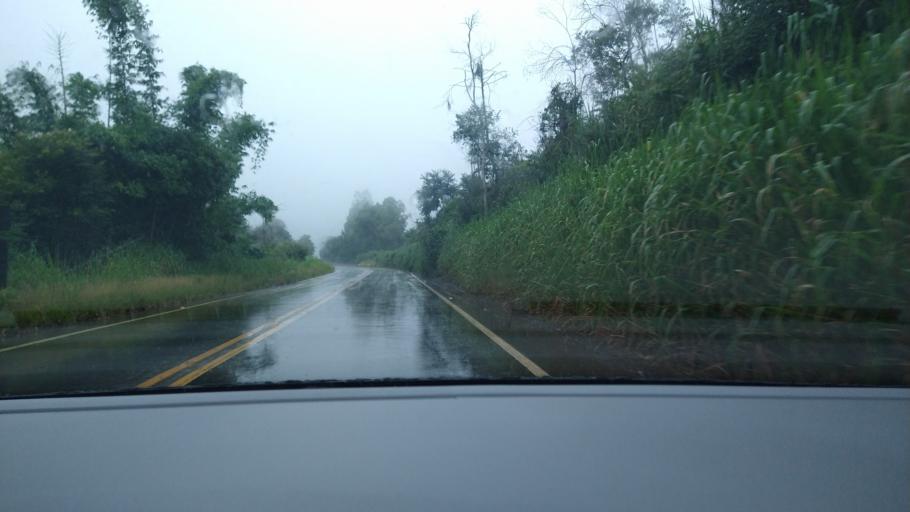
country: BR
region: Minas Gerais
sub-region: Ponte Nova
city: Ponte Nova
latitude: -20.5682
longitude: -42.8721
